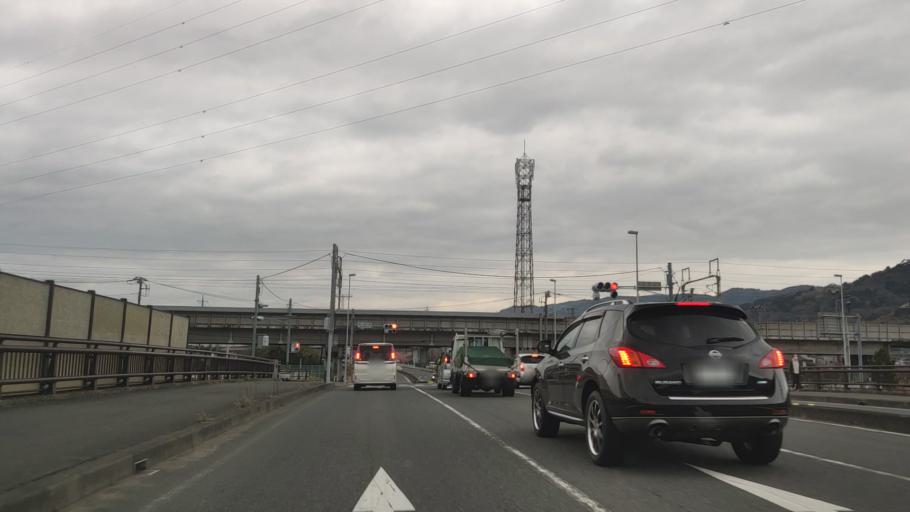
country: JP
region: Kanagawa
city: Odawara
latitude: 35.2872
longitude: 139.1996
